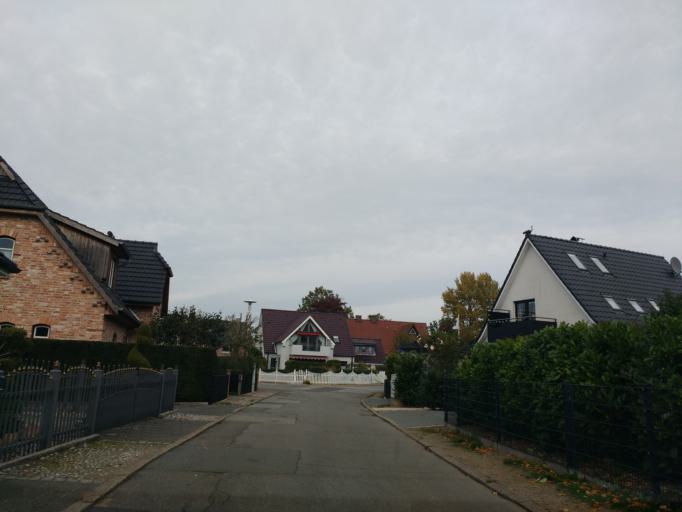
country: DE
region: Schleswig-Holstein
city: Gromitz
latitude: 54.1511
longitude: 10.9740
